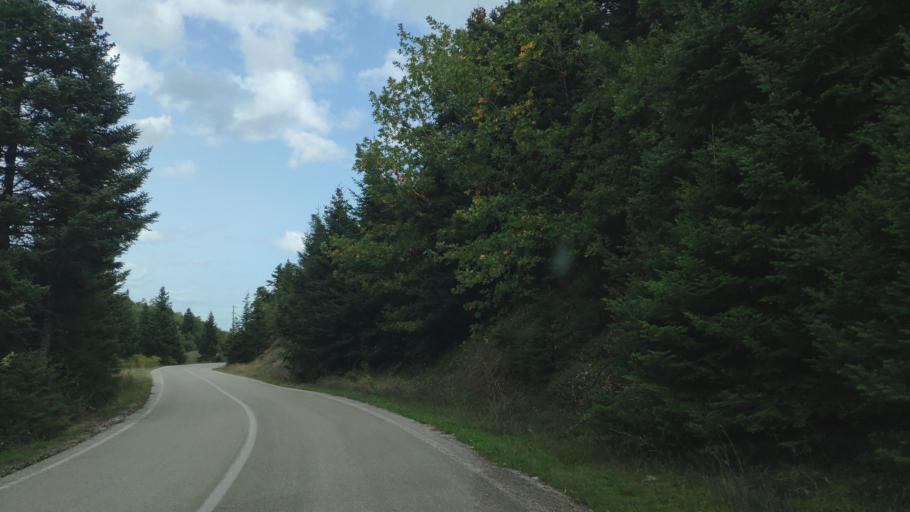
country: GR
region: Central Greece
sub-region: Nomos Fthiotidos
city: Stavros
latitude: 38.7300
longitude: 22.3548
